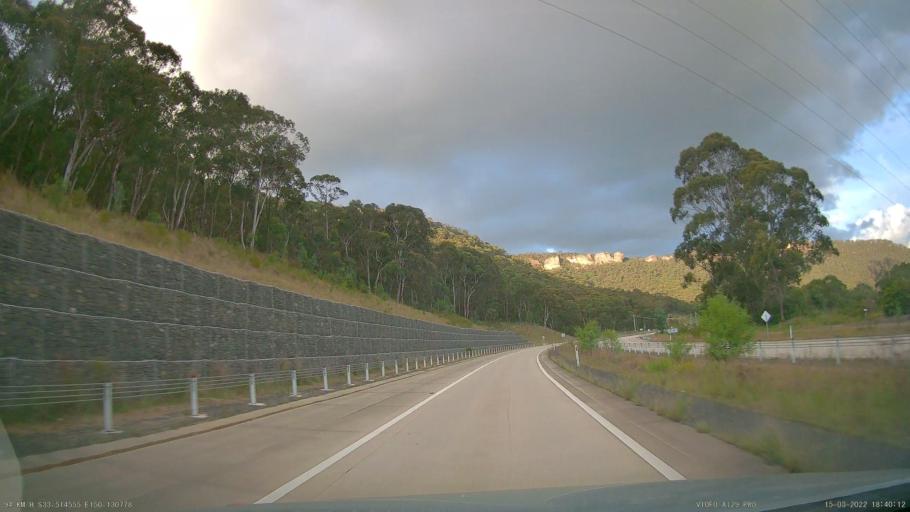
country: AU
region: New South Wales
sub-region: Lithgow
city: Bowenfels
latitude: -33.5142
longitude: 150.1314
